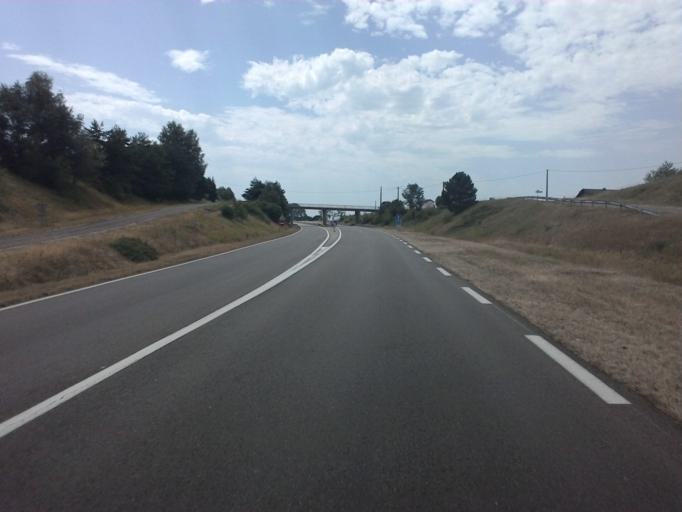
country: FR
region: Franche-Comte
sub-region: Departement du Jura
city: Saint-Amour
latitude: 46.4253
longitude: 5.3504
